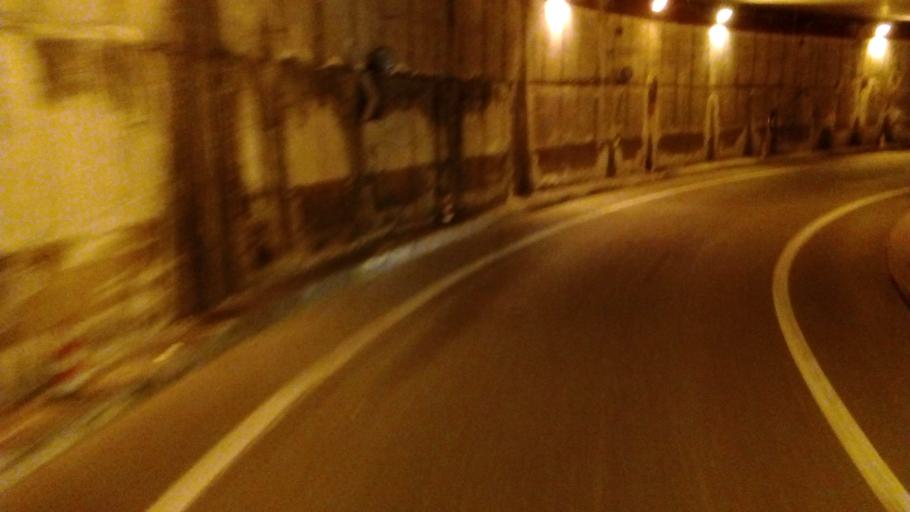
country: IT
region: Tuscany
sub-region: Provincia di Livorno
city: Quercianella
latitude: 43.4826
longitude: 10.3357
